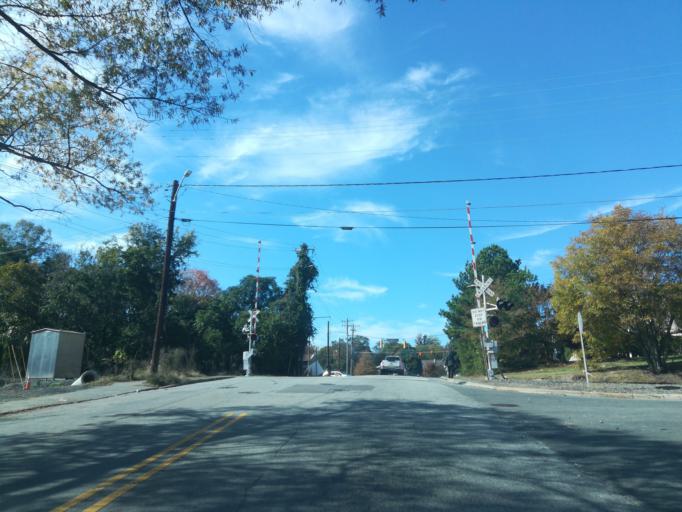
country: US
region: North Carolina
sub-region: Durham County
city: Durham
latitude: 35.9930
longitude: -78.8900
